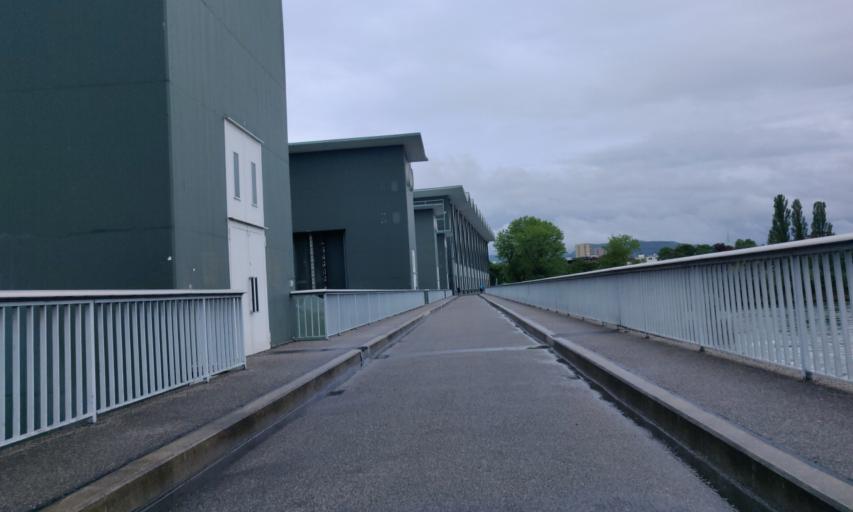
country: CH
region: Basel-Landschaft
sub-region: Bezirk Arlesheim
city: Birsfelden
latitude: 47.5614
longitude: 7.6254
